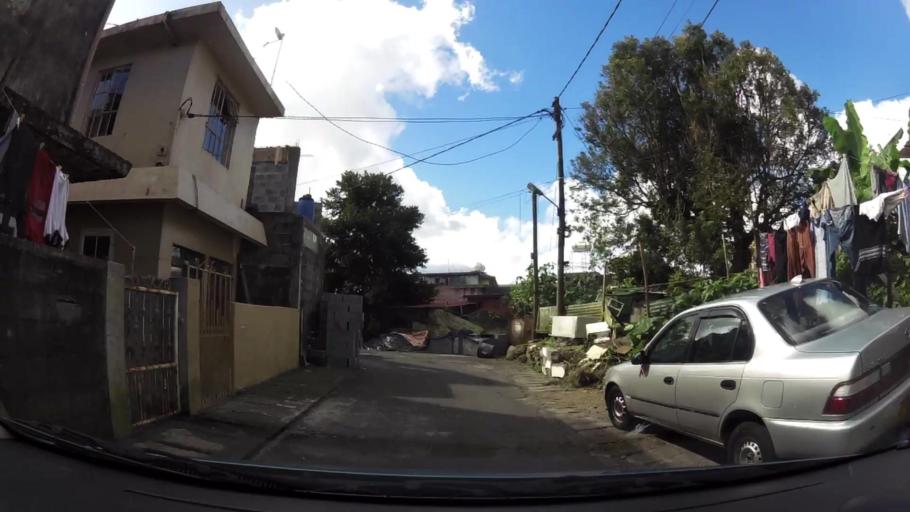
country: MU
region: Plaines Wilhems
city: Curepipe
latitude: -20.3295
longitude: 57.5217
